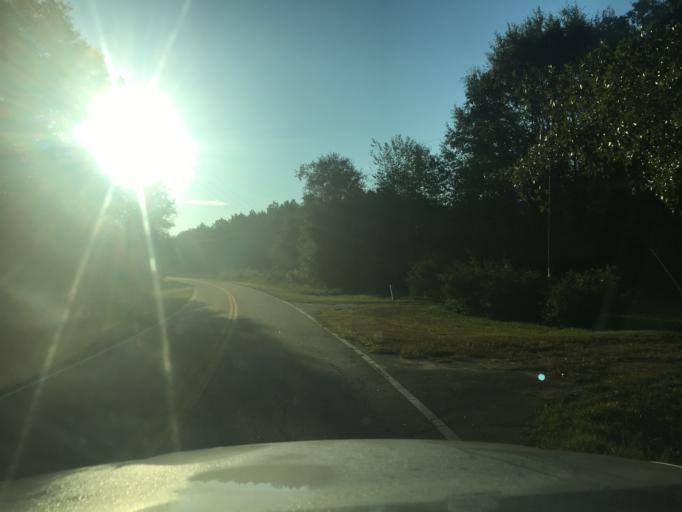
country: US
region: South Carolina
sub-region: Spartanburg County
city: Woodruff
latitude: 34.7875
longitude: -82.0020
